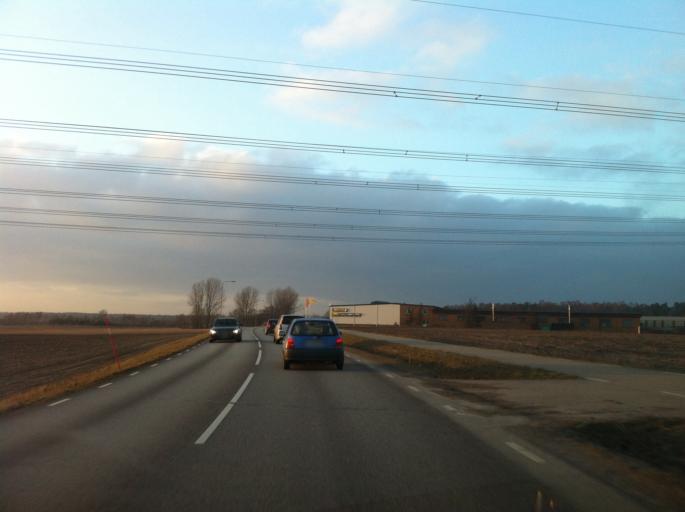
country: SE
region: Skane
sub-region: Kavlinge Kommun
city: Loddekopinge
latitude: 55.7866
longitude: 13.0042
